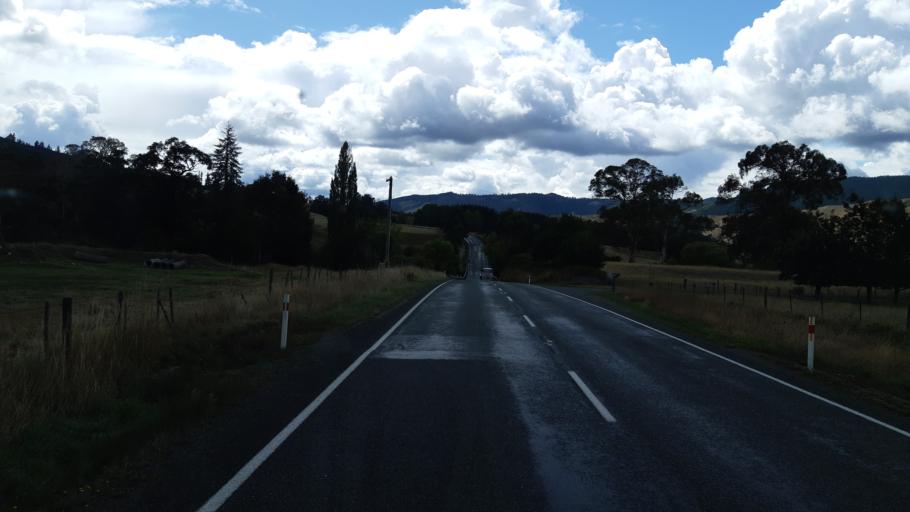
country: NZ
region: Tasman
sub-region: Tasman District
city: Wakefield
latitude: -41.5608
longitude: 172.7820
